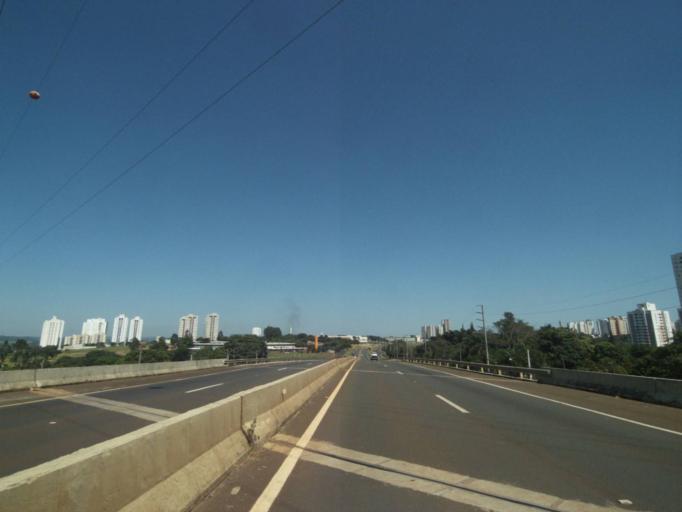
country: BR
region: Parana
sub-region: Londrina
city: Londrina
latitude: -23.3473
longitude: -51.1720
